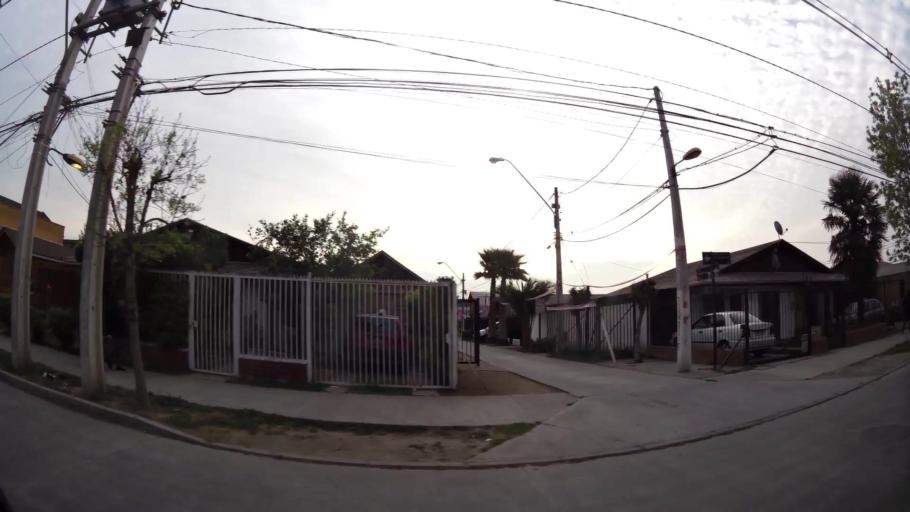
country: CL
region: Santiago Metropolitan
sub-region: Provincia de Santiago
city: Lo Prado
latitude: -33.5266
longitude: -70.7970
